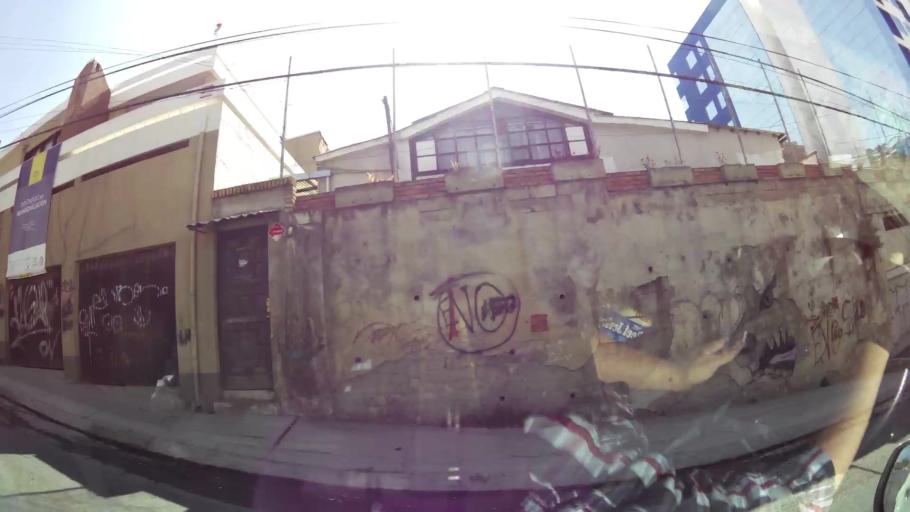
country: BO
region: La Paz
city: La Paz
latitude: -16.5255
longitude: -68.1079
